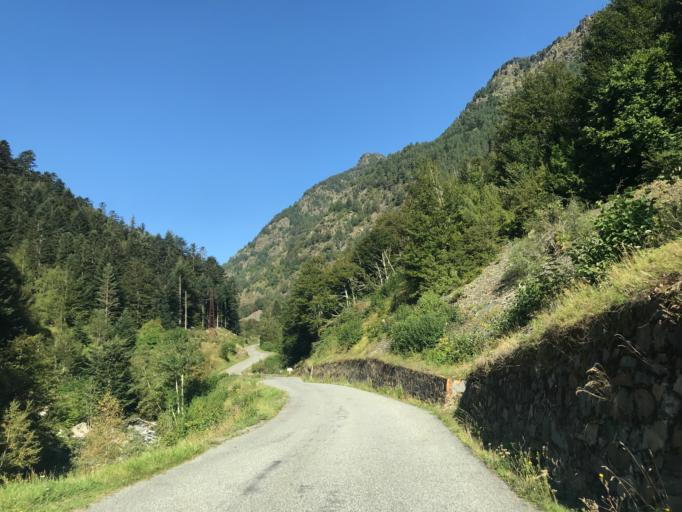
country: FR
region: Midi-Pyrenees
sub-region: Departement des Hautes-Pyrenees
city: Saint-Lary-Soulan
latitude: 42.8130
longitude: 0.2192
